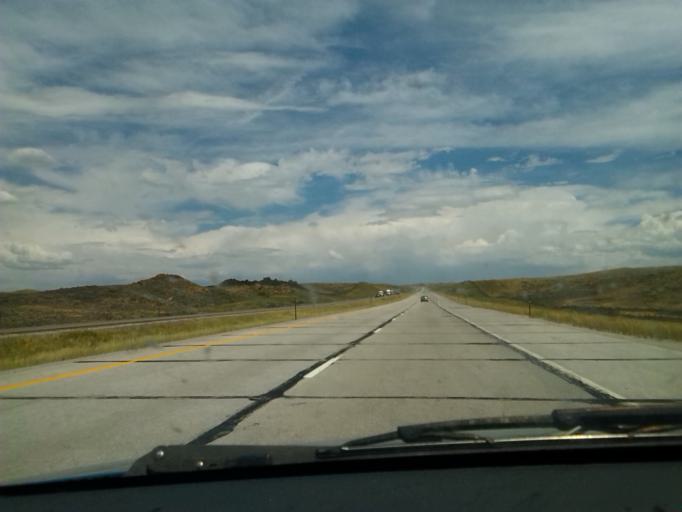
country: US
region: Wyoming
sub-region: Carbon County
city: Saratoga
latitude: 41.7305
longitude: -106.6943
